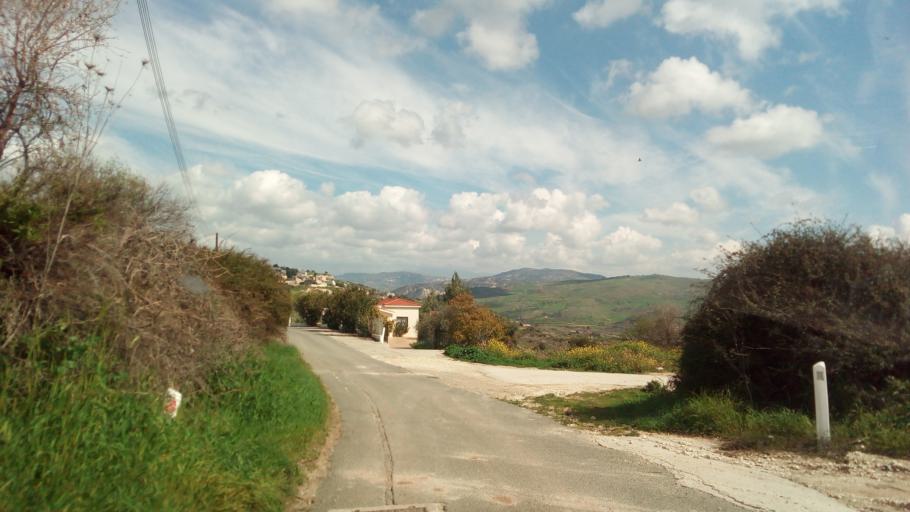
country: CY
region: Pafos
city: Mesogi
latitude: 34.7710
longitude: 32.5626
